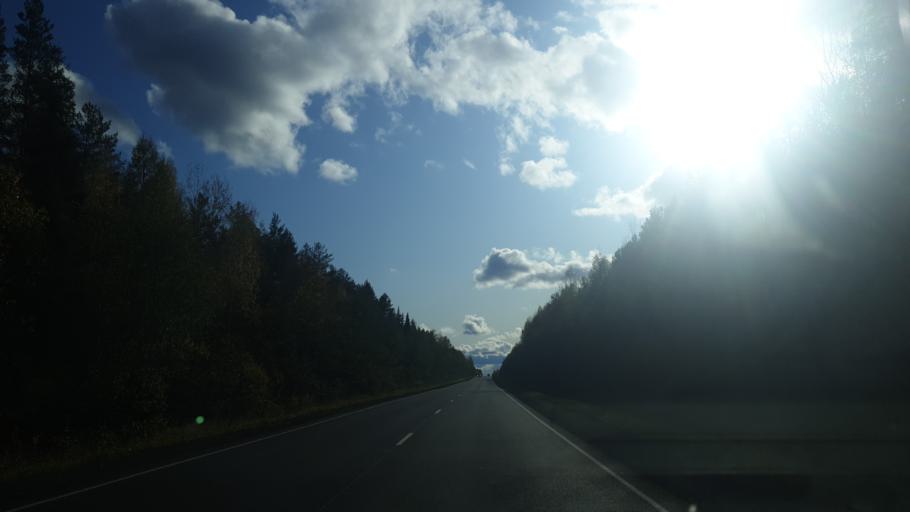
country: RU
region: Komi Republic
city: Letka
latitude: 60.3583
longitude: 49.6723
